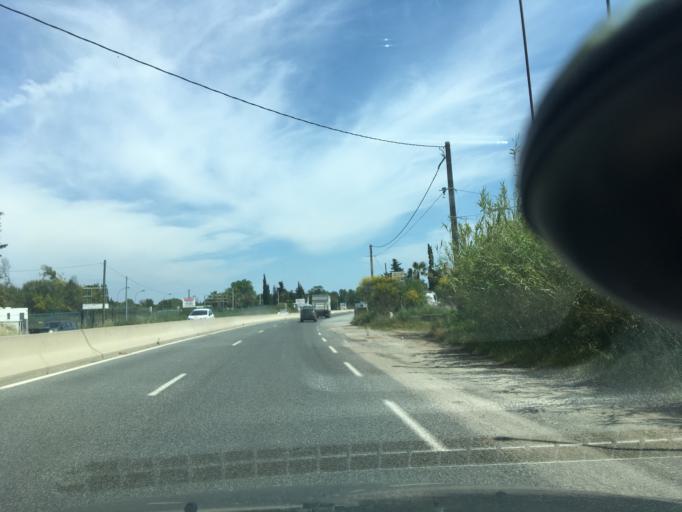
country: FR
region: Provence-Alpes-Cote d'Azur
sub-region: Departement du Var
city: Roquebrune-sur-Argens
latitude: 43.4636
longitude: 6.6413
